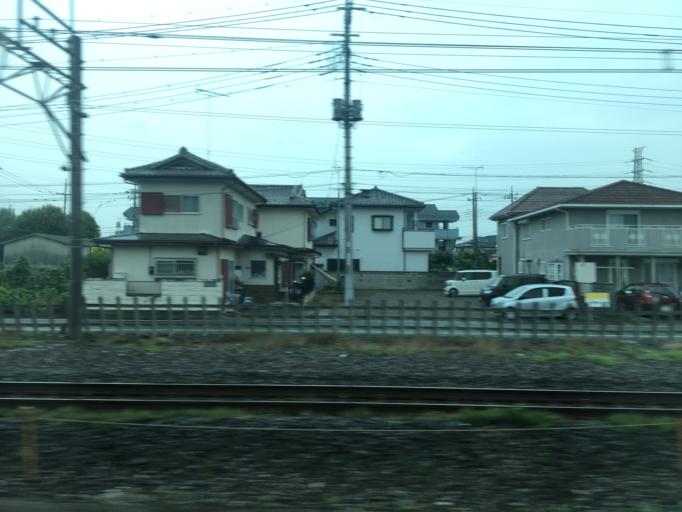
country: JP
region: Tochigi
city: Oyama
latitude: 36.2557
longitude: 139.7592
